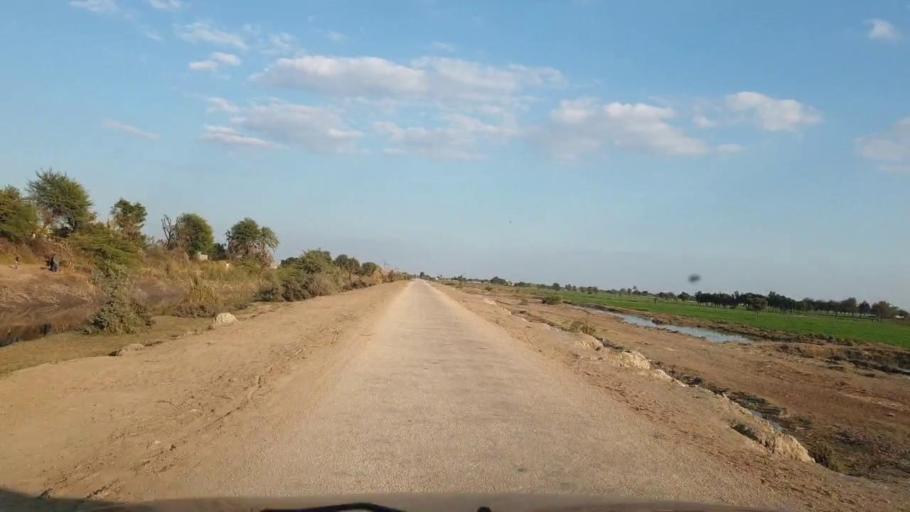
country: PK
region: Sindh
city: Sinjhoro
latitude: 25.9941
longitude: 68.7546
